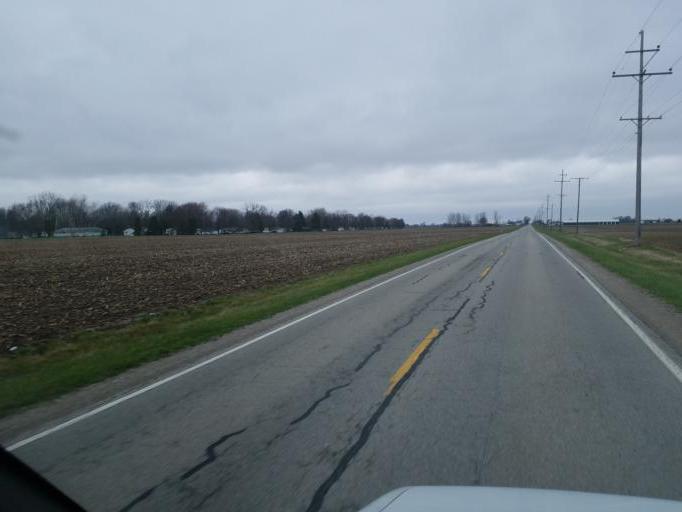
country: US
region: Ohio
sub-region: Marion County
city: Marion
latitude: 40.6435
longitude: -83.0732
